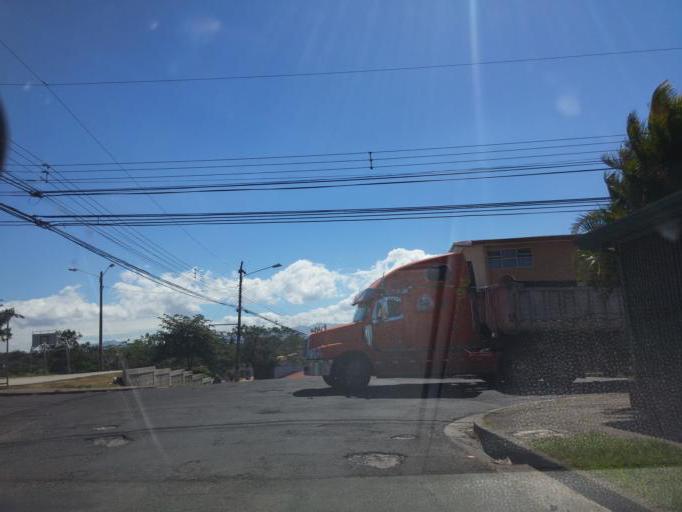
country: CR
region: Alajuela
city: Alajuela
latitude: 10.0064
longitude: -84.2041
